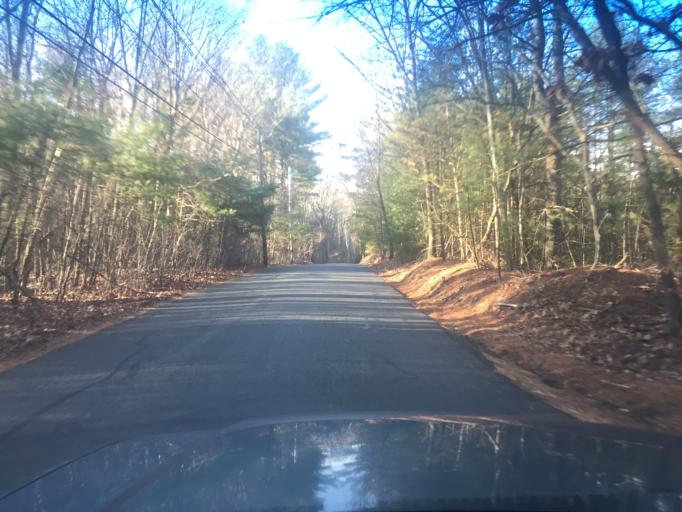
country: US
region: Massachusetts
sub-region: Middlesex County
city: Ashland
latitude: 42.2263
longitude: -71.4782
